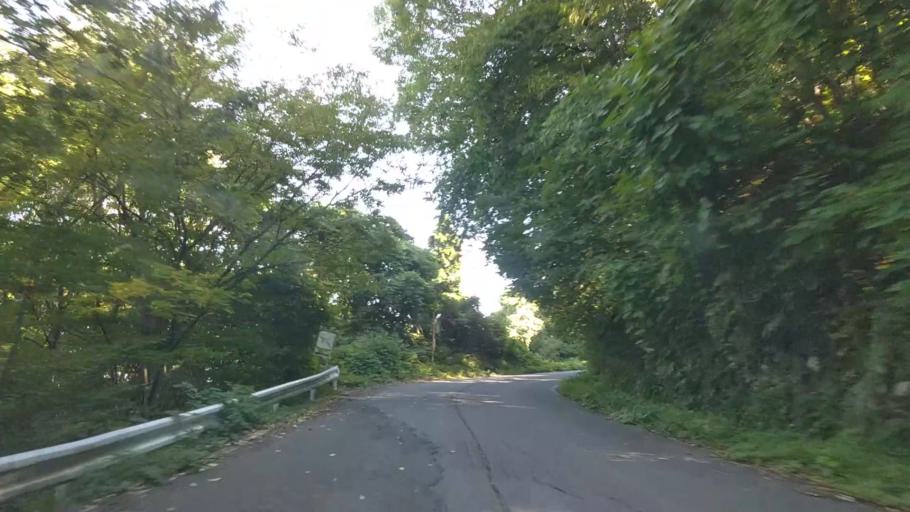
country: JP
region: Nagano
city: Nagano-shi
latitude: 36.5828
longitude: 138.0985
